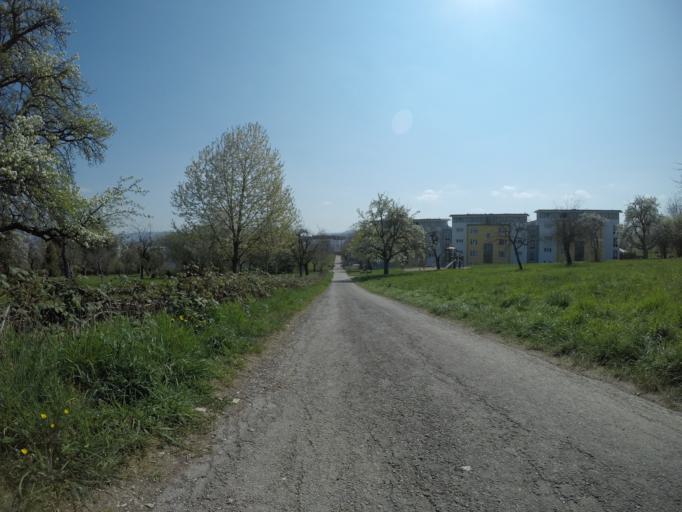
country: DE
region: Baden-Wuerttemberg
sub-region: Tuebingen Region
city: Reutlingen
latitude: 48.4871
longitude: 9.1807
